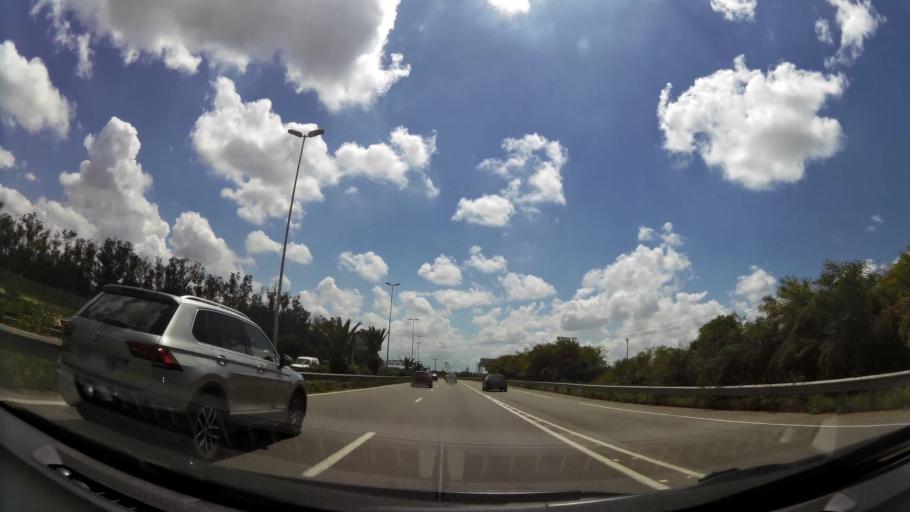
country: MA
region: Grand Casablanca
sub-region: Nouaceur
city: Bouskoura
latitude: 33.4817
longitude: -7.6332
